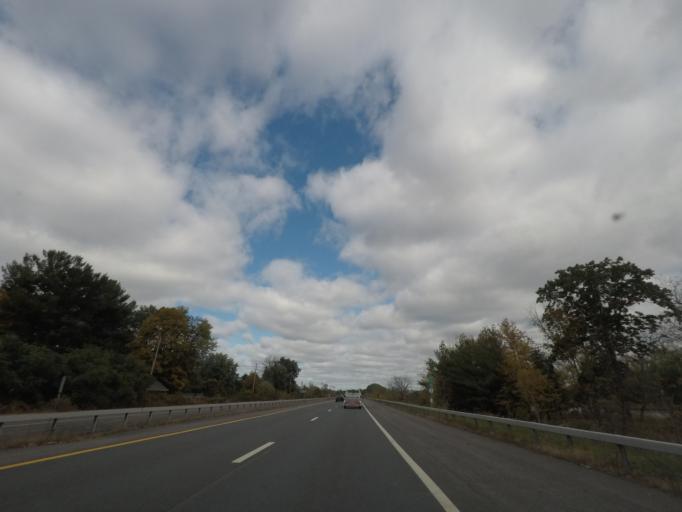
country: US
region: New York
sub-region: Albany County
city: Green Island
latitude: 42.7545
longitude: -73.6987
